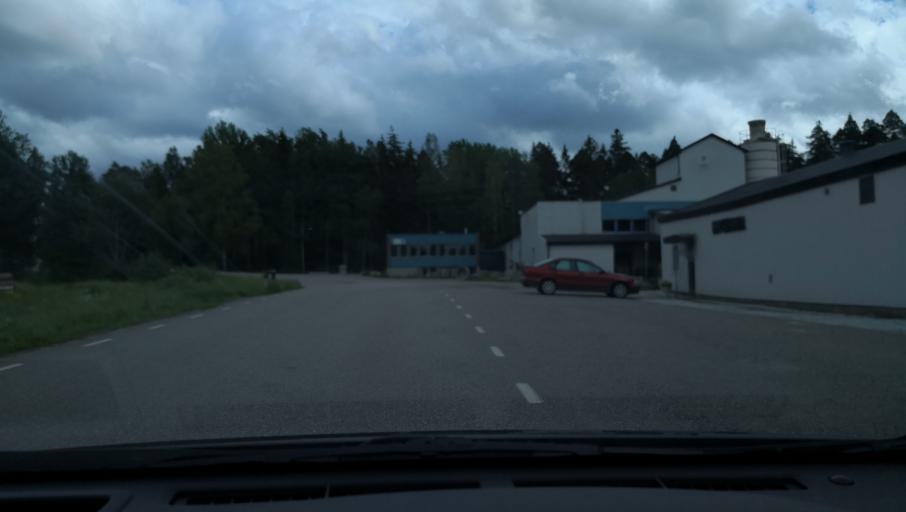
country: SE
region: OErebro
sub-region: Lindesbergs Kommun
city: Fellingsbro
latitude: 59.3282
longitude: 15.6731
